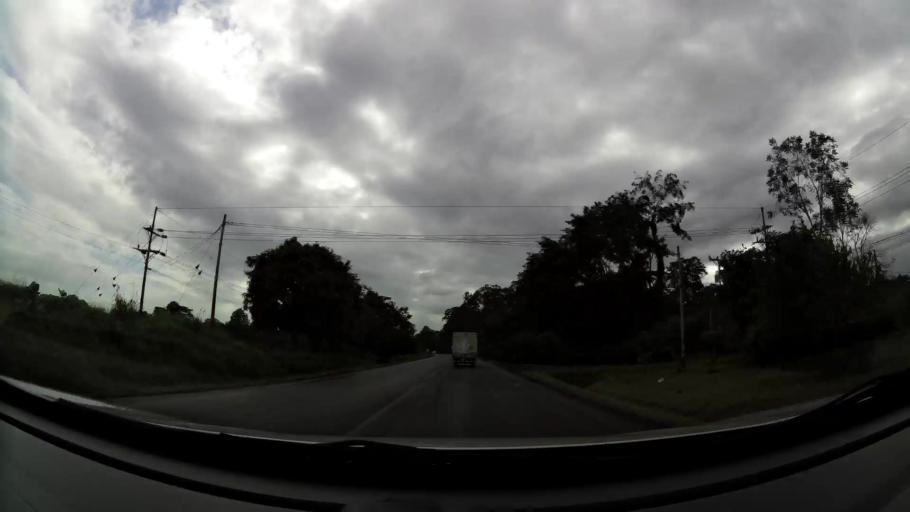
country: CR
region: Limon
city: Pocora
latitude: 10.1556
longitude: -83.5943
